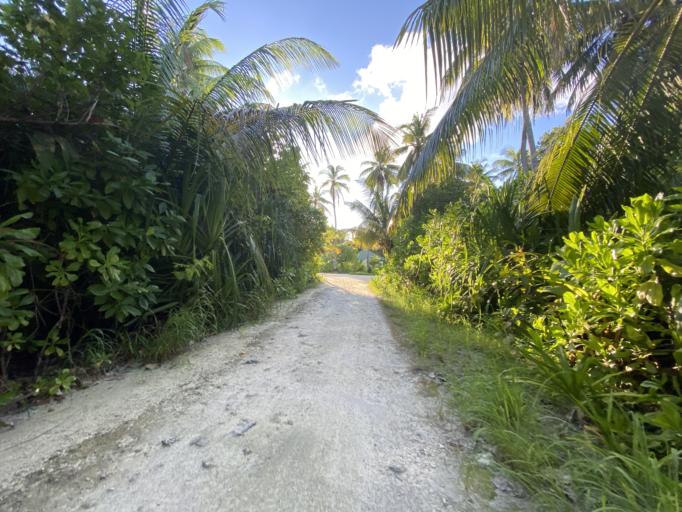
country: MV
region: Seenu
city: Meedhoo
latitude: -0.6134
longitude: 73.2250
